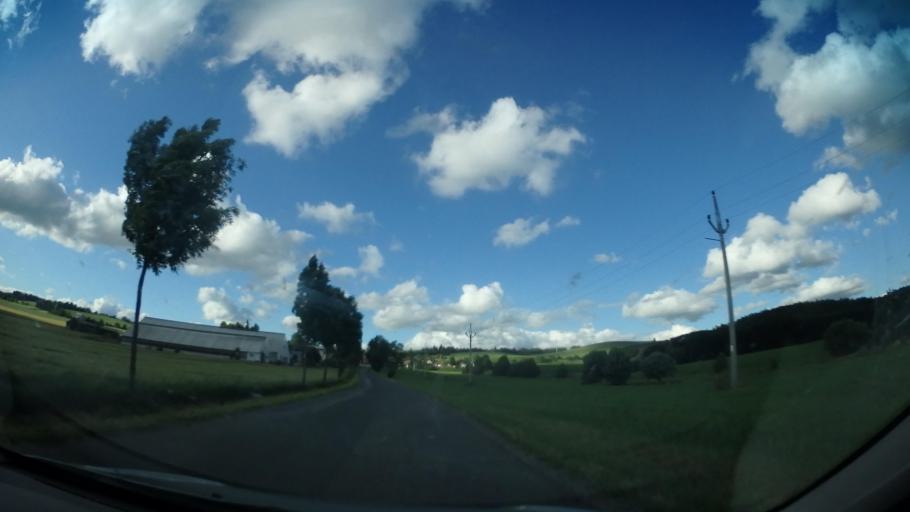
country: CZ
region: Vysocina
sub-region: Okres Zd'ar nad Sazavou
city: Jimramov
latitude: 49.5715
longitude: 16.1865
